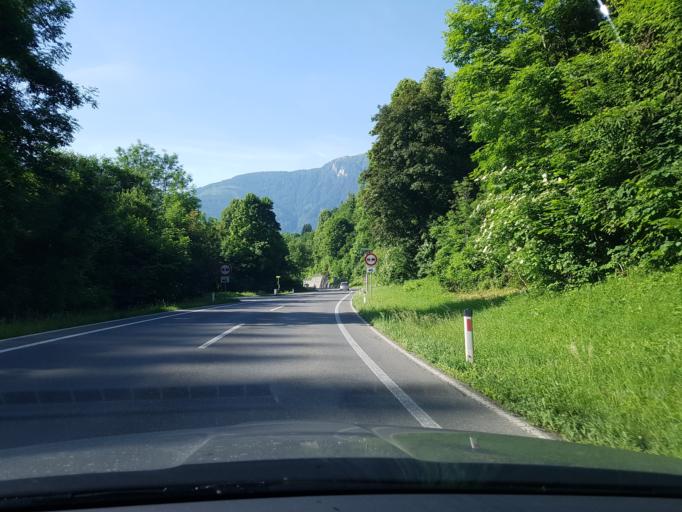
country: AT
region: Carinthia
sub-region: Politischer Bezirk Spittal an der Drau
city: Spittal an der Drau
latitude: 46.8071
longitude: 13.4962
